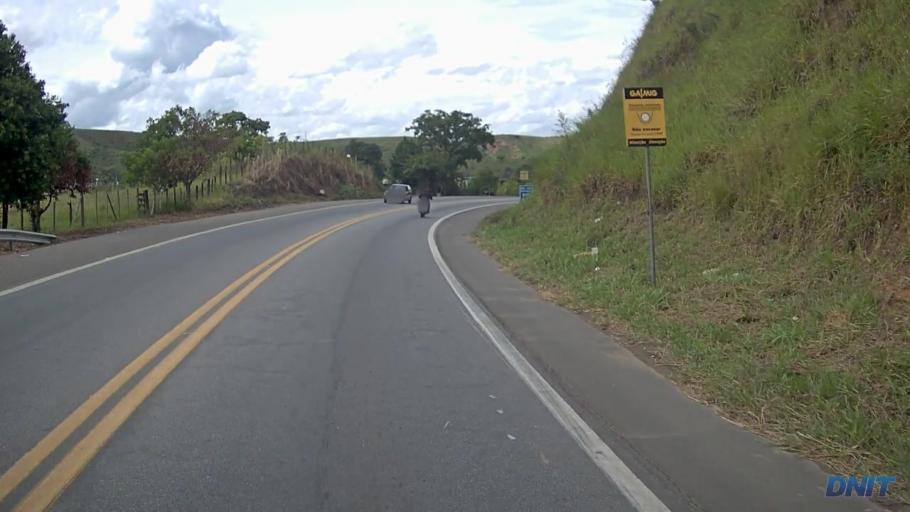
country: BR
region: Minas Gerais
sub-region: Ipatinga
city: Ipatinga
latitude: -19.4581
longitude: -42.5252
